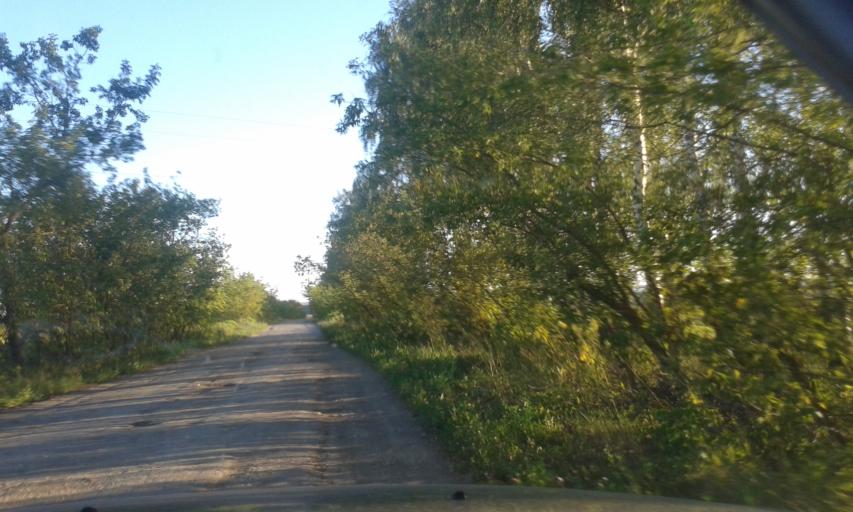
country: RU
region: Tula
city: Krapivna
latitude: 54.1292
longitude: 37.1564
